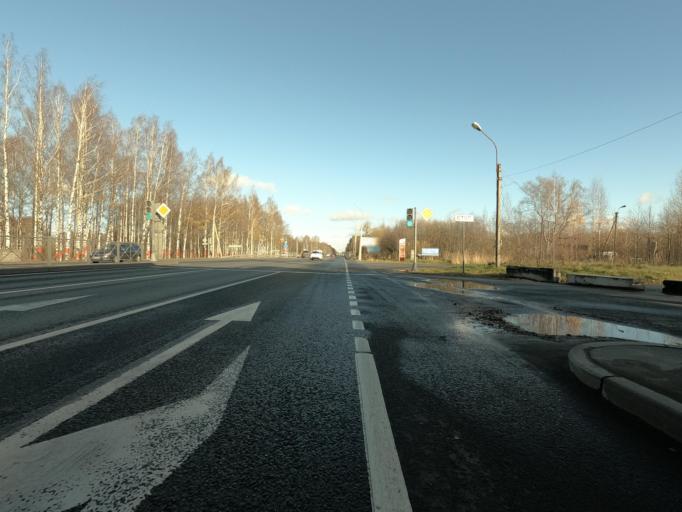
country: RU
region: St.-Petersburg
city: Krasnogvargeisky
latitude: 59.9940
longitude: 30.5387
